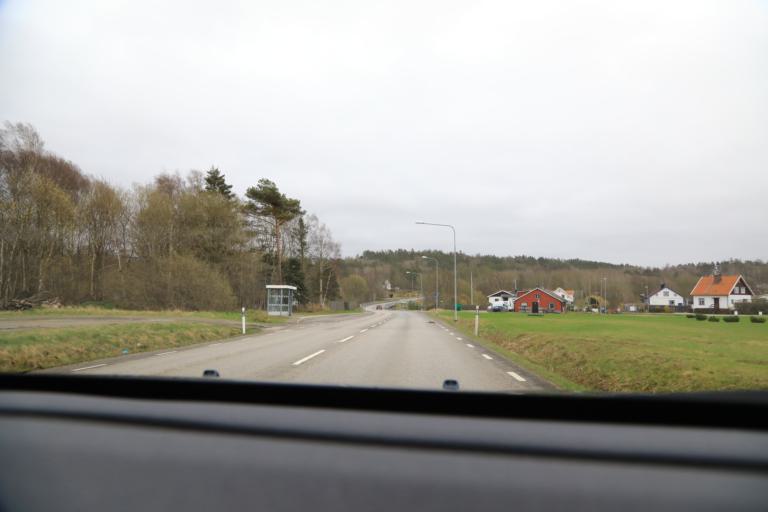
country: SE
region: Halland
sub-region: Kungsbacka Kommun
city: Frillesas
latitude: 57.3135
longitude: 12.1789
